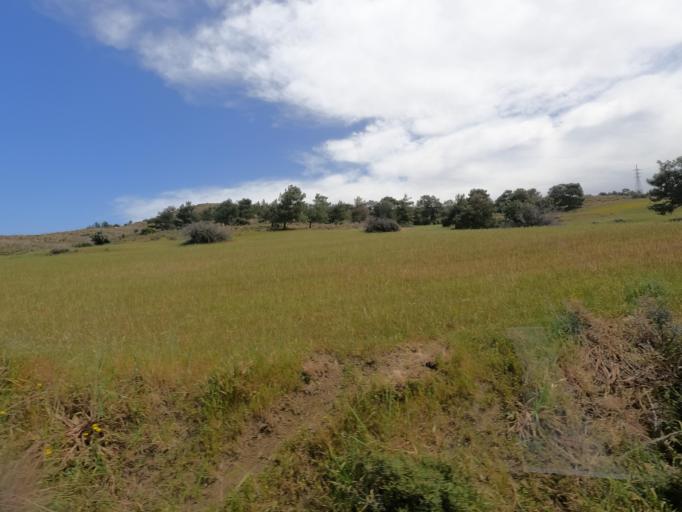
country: CY
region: Lefkosia
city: Lefka
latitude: 35.0752
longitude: 32.9289
